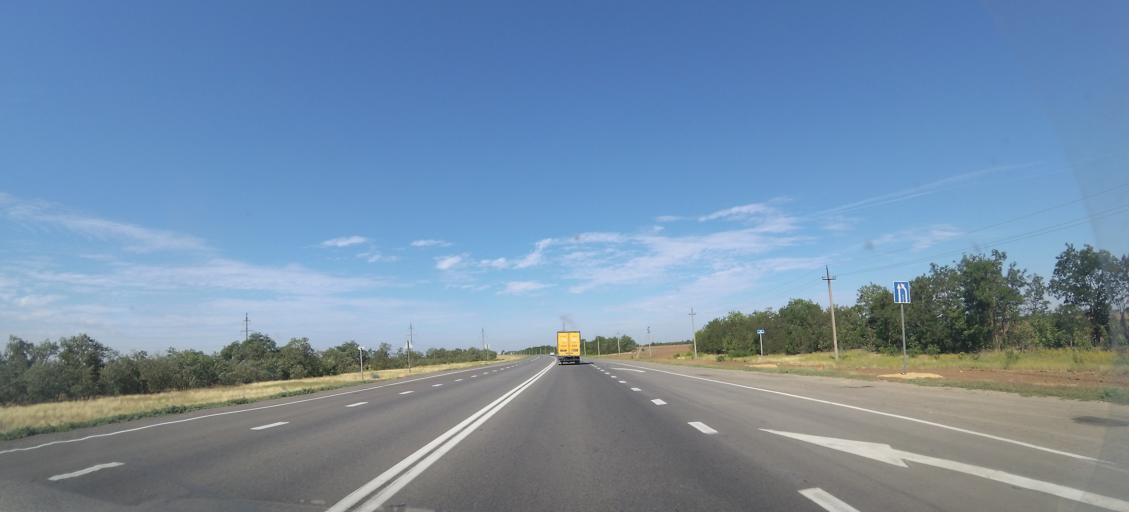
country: RU
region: Volgograd
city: Oktyabr'skiy
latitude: 48.6984
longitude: 43.8065
